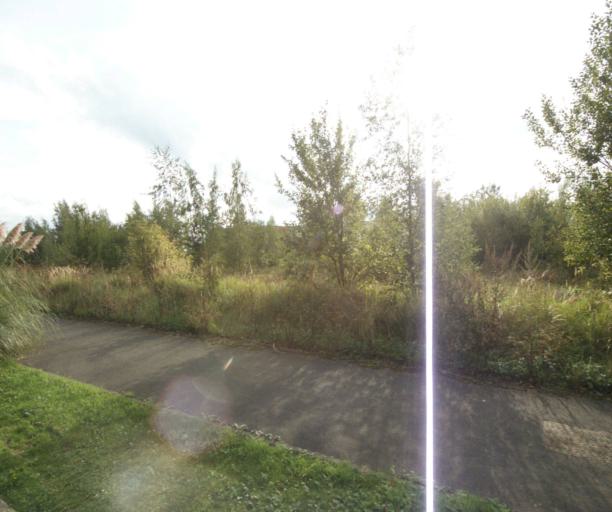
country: FR
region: Nord-Pas-de-Calais
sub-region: Departement du Nord
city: Wavrin
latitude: 50.5569
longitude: 2.9377
